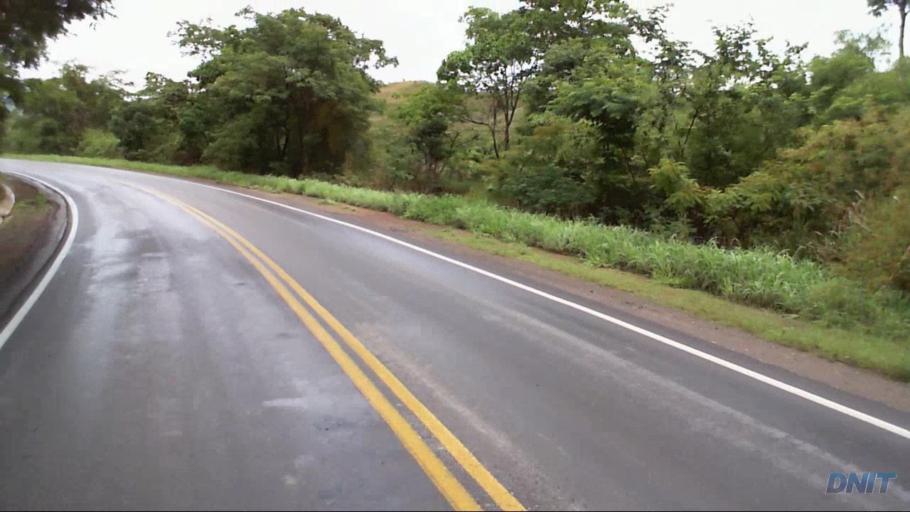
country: BR
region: Goias
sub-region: Padre Bernardo
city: Padre Bernardo
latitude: -15.4954
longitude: -48.2223
